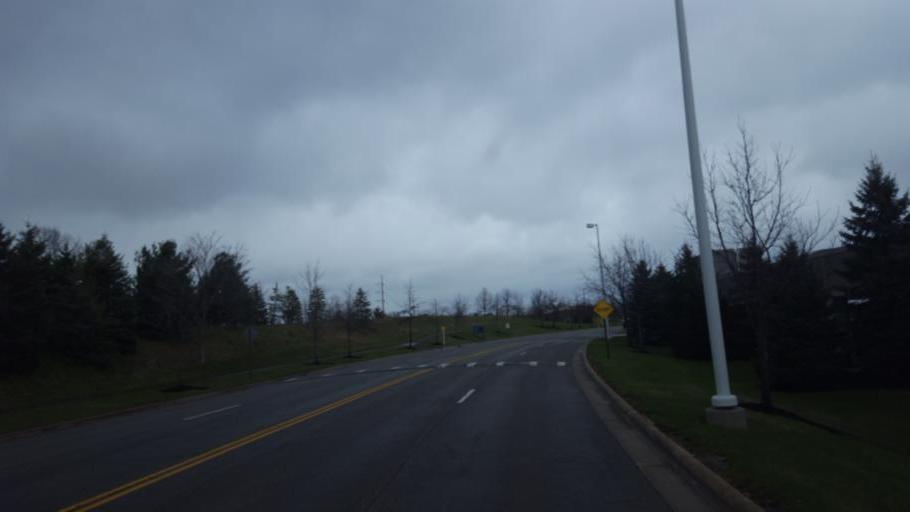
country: US
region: Ohio
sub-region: Franklin County
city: Worthington
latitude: 40.1420
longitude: -83.0003
